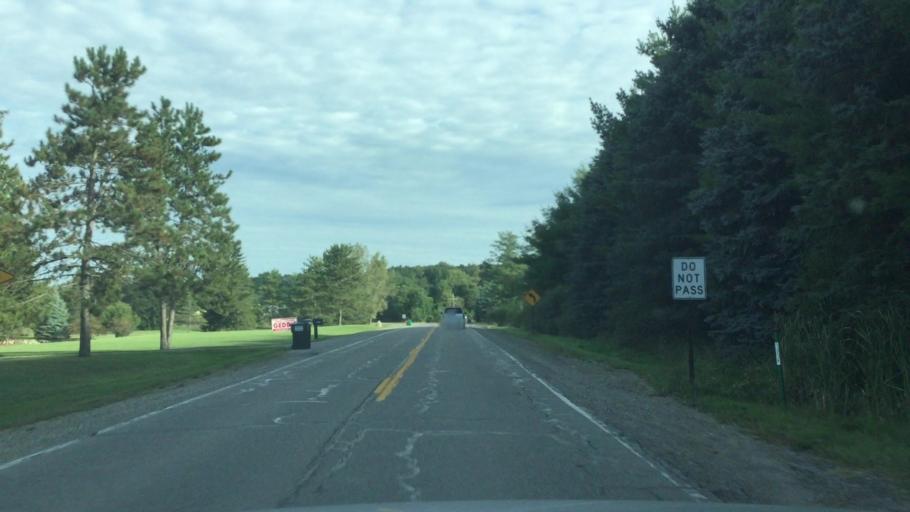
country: US
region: Michigan
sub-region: Livingston County
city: Howell
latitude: 42.5708
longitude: -83.8930
